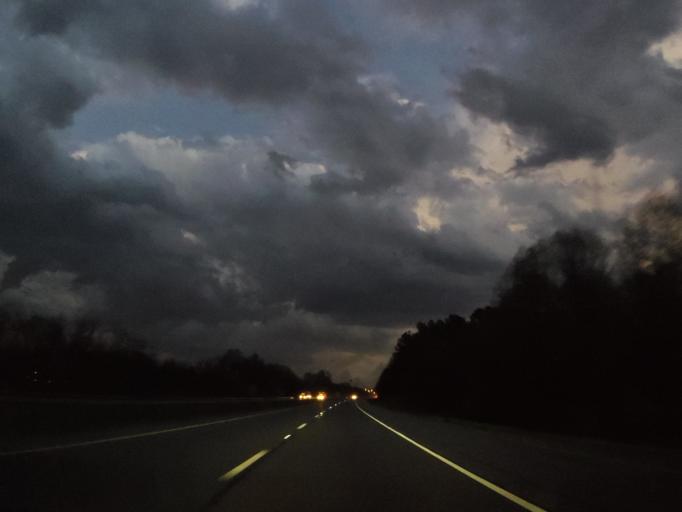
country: US
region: Tennessee
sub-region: Putnam County
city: Cookeville
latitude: 36.1359
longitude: -85.4633
